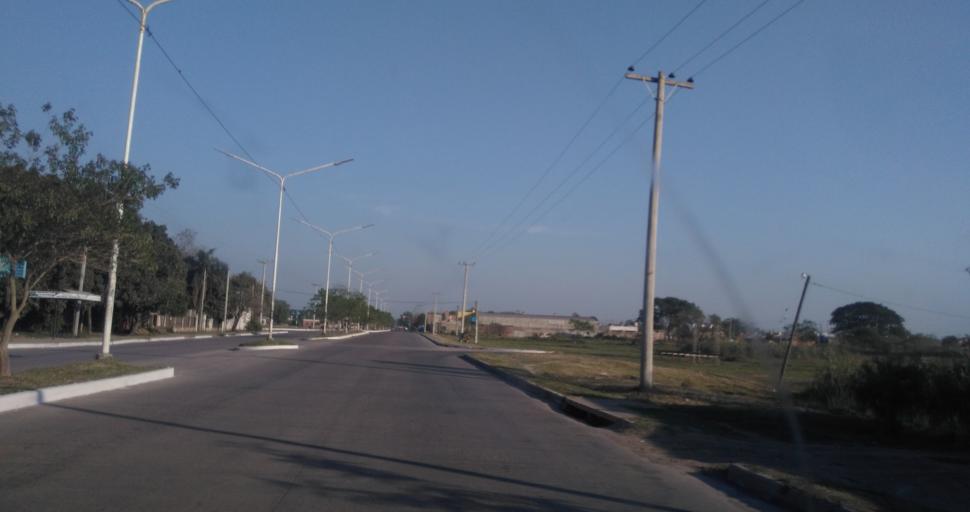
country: AR
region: Chaco
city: Fontana
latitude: -27.4153
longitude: -59.0268
